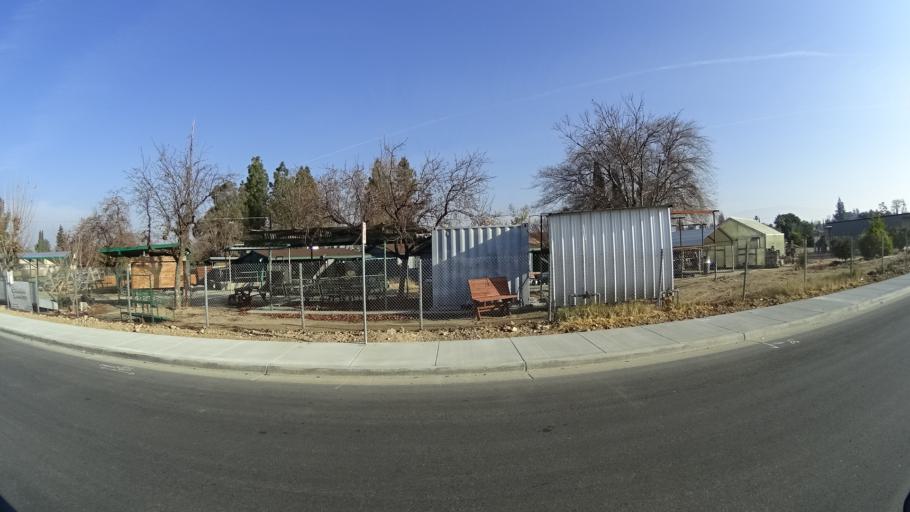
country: US
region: California
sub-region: Kern County
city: Oildale
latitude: 35.4023
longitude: -118.9321
